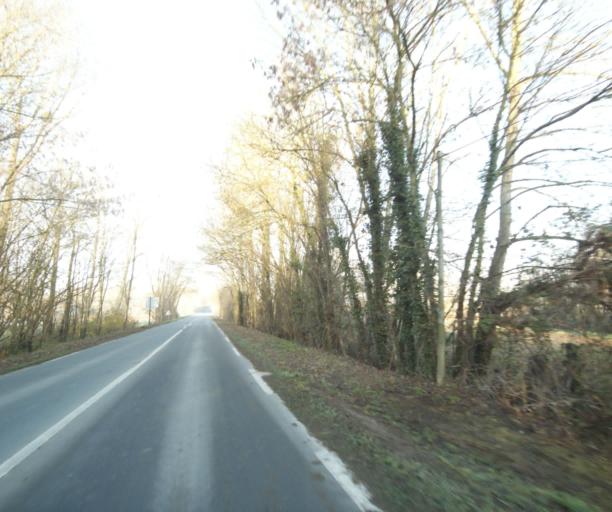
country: FR
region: Poitou-Charentes
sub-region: Departement de la Charente-Maritime
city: Cherac
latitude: 45.6856
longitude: -0.4549
